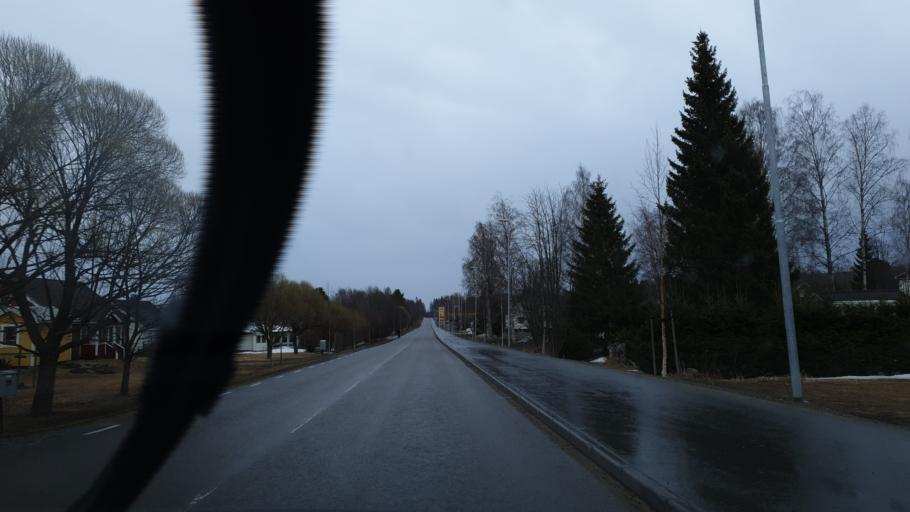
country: SE
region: Vaesterbotten
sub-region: Skelleftea Kommun
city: Kage
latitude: 64.8319
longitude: 20.9925
